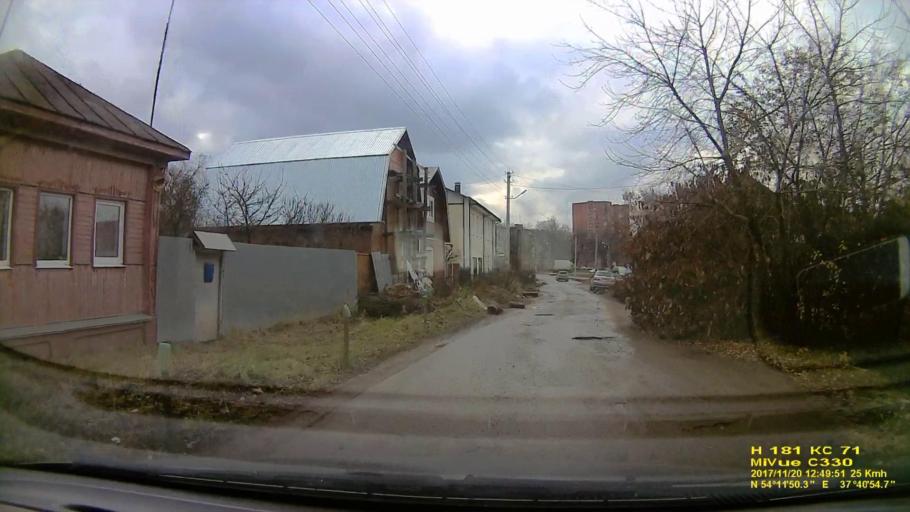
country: RU
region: Tula
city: Tula
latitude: 54.1973
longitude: 37.6818
